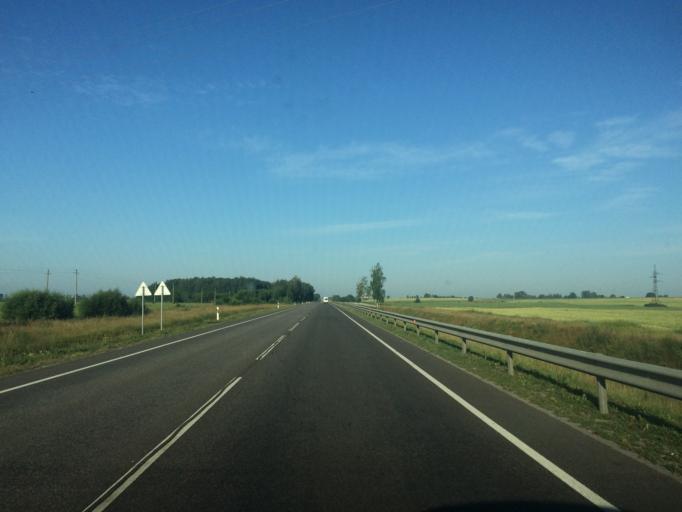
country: LT
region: Vilnius County
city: Ukmerge
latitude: 55.2340
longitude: 24.7197
